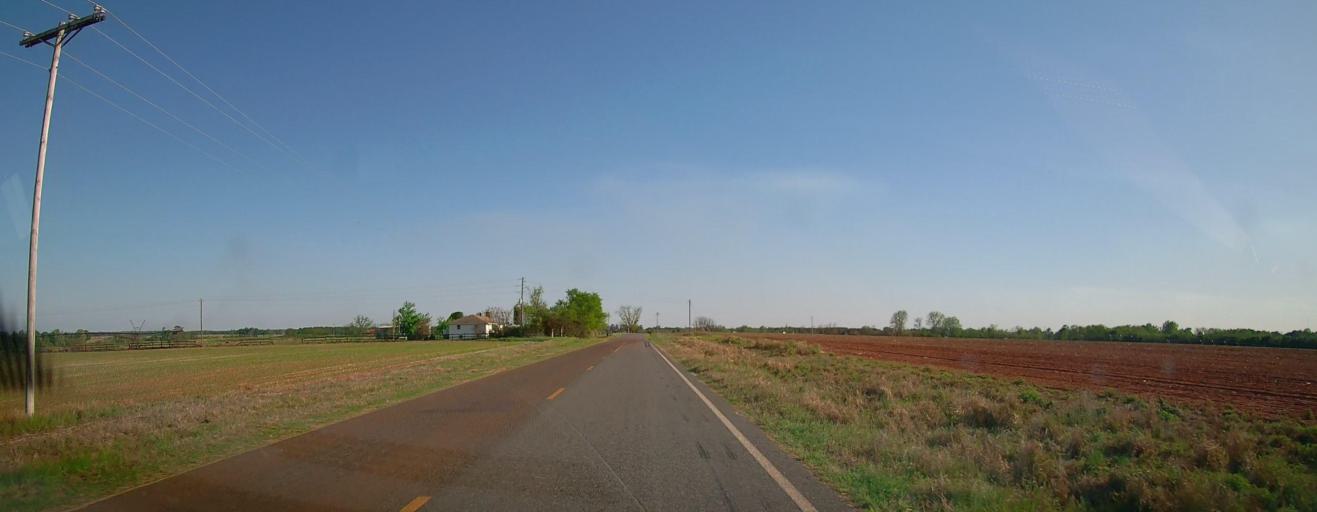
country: US
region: Georgia
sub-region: Macon County
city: Montezuma
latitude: 32.3430
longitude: -83.9438
